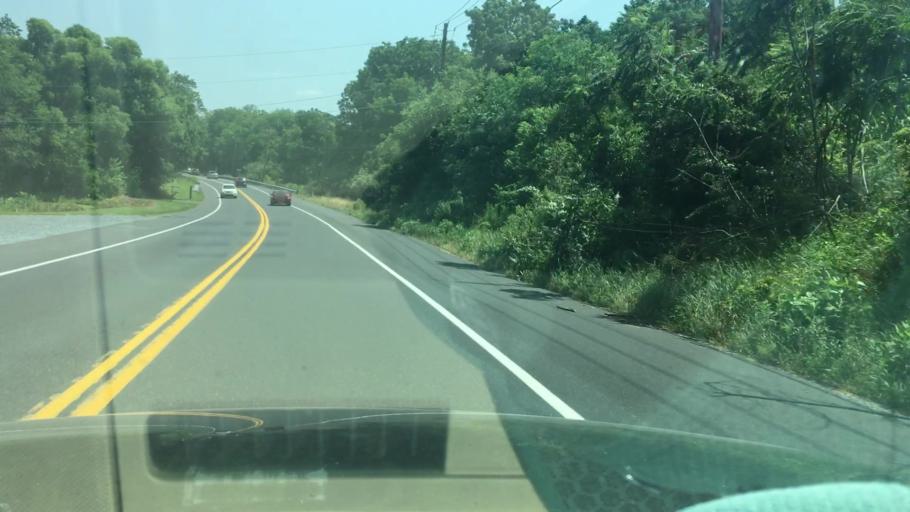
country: US
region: Pennsylvania
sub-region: Lehigh County
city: Schnecksville
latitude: 40.6799
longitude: -75.7004
